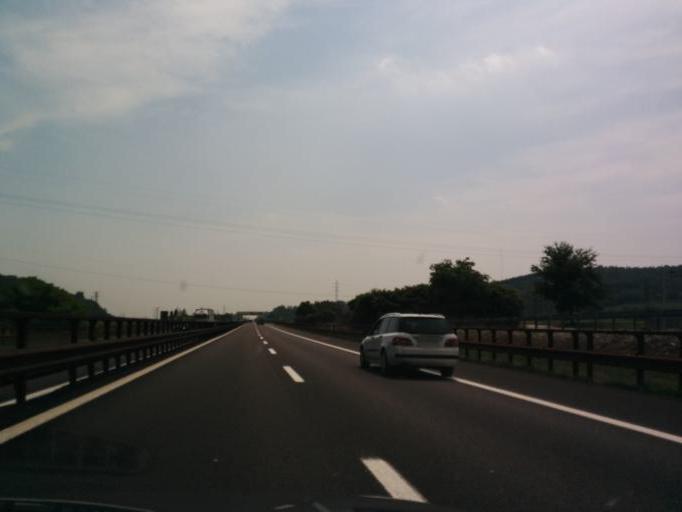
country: IT
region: Veneto
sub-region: Provincia di Verona
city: Rivoli Veronese
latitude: 45.5651
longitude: 10.8020
